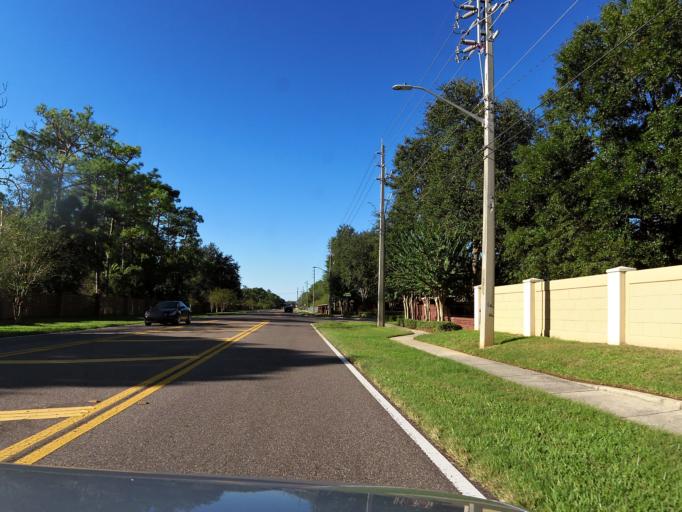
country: US
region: Florida
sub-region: Duval County
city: Neptune Beach
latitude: 30.3109
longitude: -81.4467
